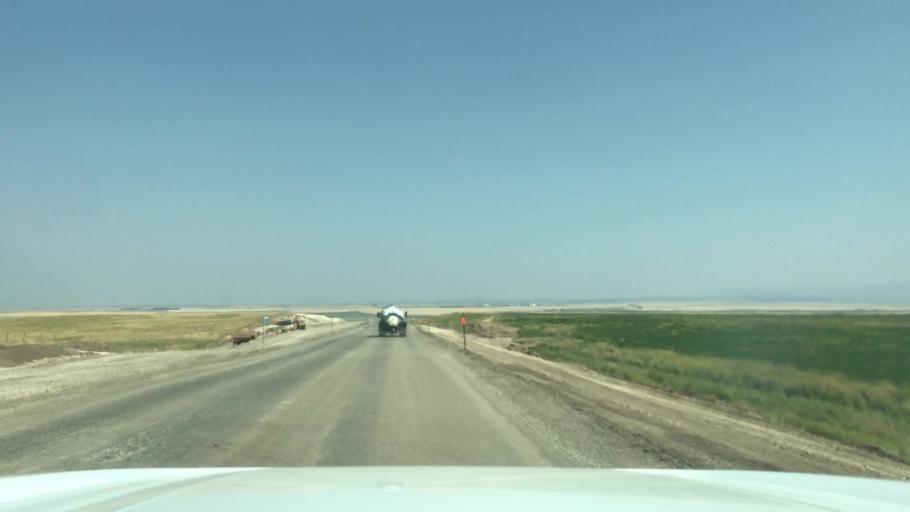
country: US
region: Montana
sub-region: Fergus County
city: Lewistown
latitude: 46.9987
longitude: -109.8154
